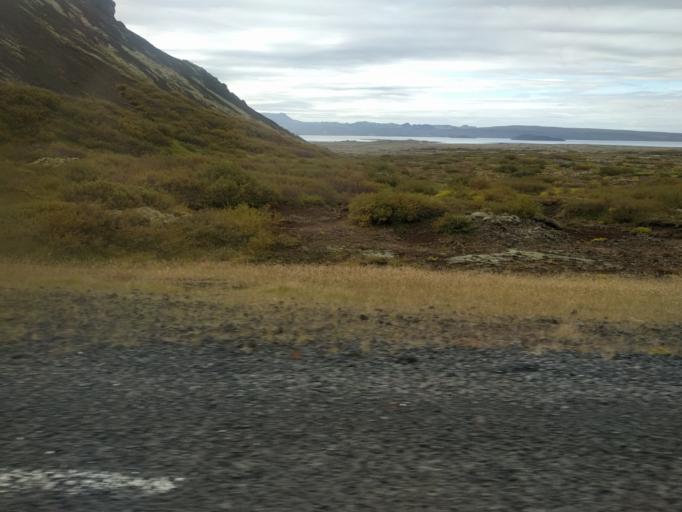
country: IS
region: South
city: Hveragerdi
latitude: 64.1987
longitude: -21.0309
